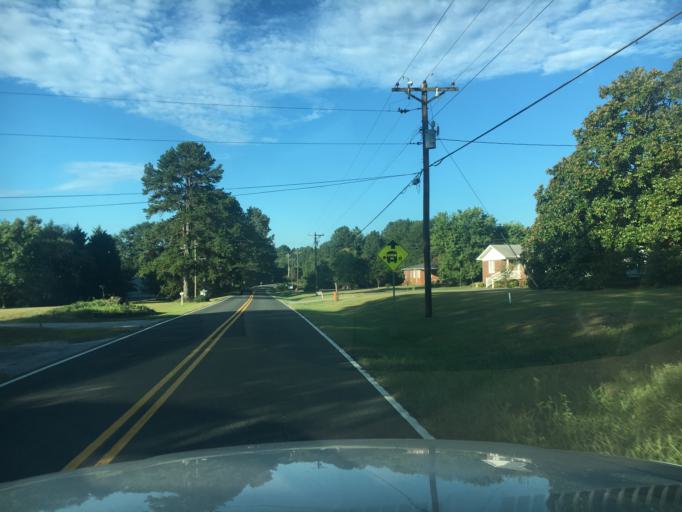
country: US
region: South Carolina
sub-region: Spartanburg County
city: Woodruff
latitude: 34.6248
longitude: -82.0700
